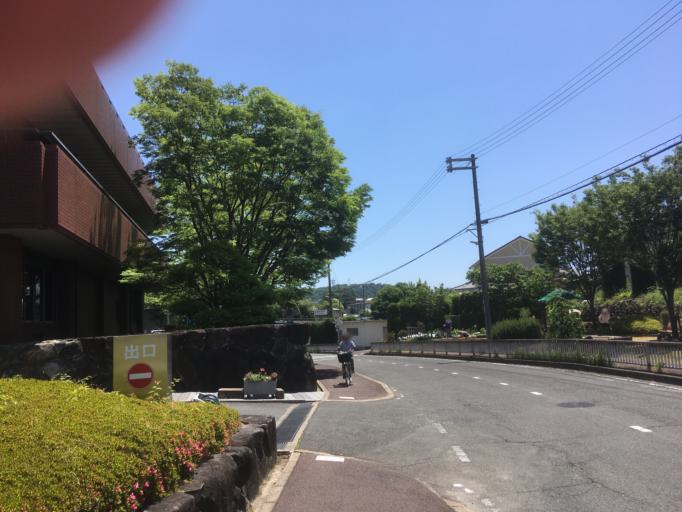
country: JP
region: Nara
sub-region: Ikoma-shi
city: Ikoma
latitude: 34.6916
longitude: 135.7005
